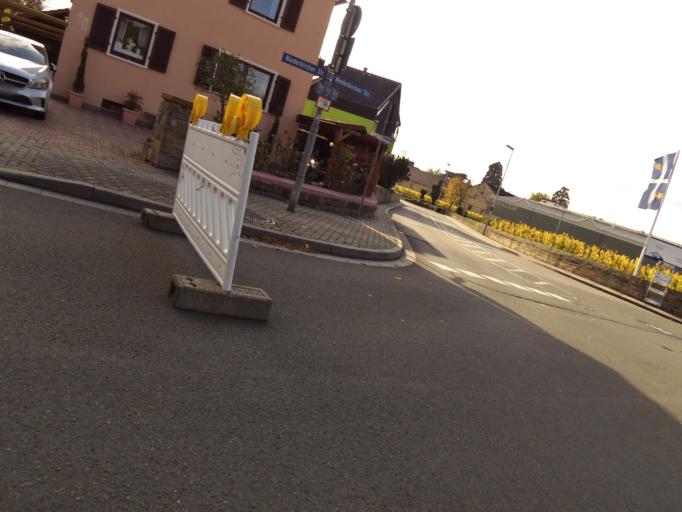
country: DE
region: Rheinland-Pfalz
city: Deidesheim
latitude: 49.4106
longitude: 8.1915
